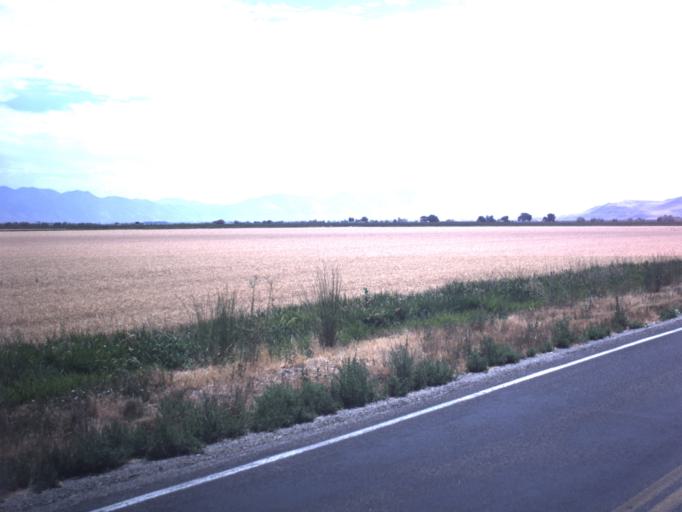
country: US
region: Utah
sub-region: Box Elder County
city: Tremonton
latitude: 41.7091
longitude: -112.2782
